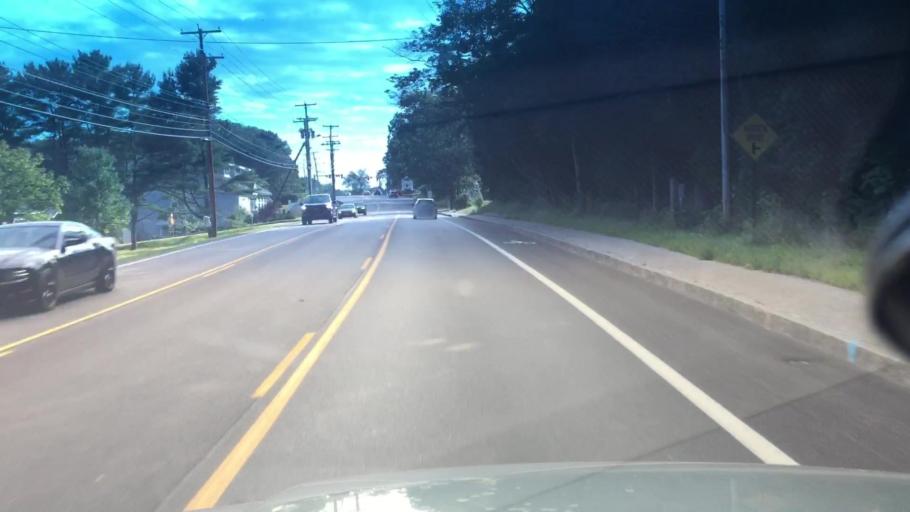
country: US
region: Maine
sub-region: Cumberland County
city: Freeport
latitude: 43.8459
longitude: -70.1152
